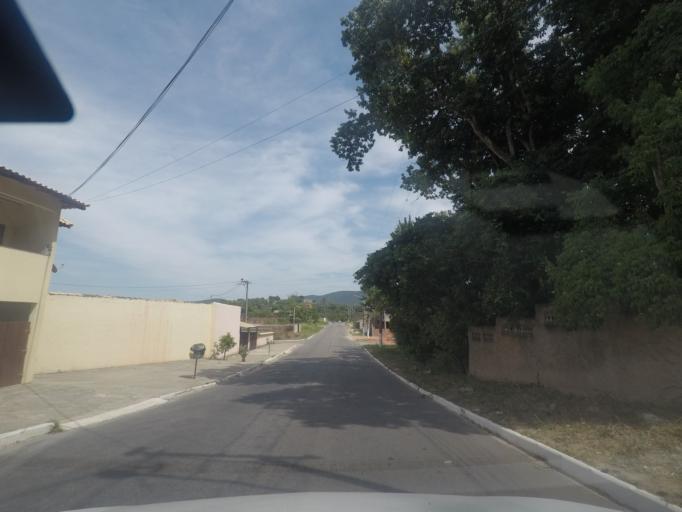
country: BR
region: Rio de Janeiro
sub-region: Marica
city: Marica
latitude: -22.9483
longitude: -42.7515
